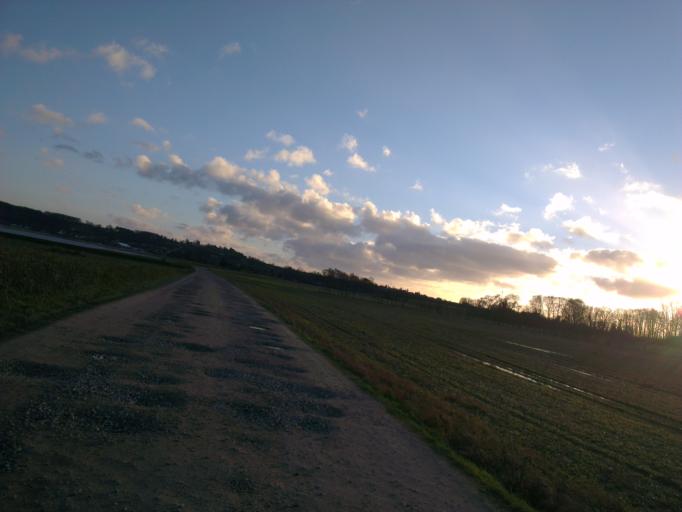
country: DK
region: Capital Region
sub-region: Frederikssund Kommune
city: Jaegerspris
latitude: 55.8658
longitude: 11.9947
